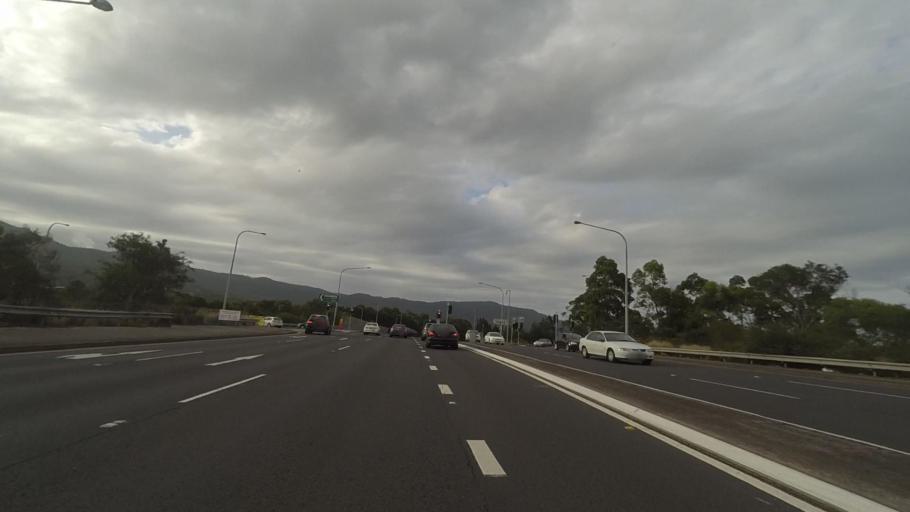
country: AU
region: New South Wales
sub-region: Wollongong
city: Gwynneville
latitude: -34.4088
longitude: 150.8916
